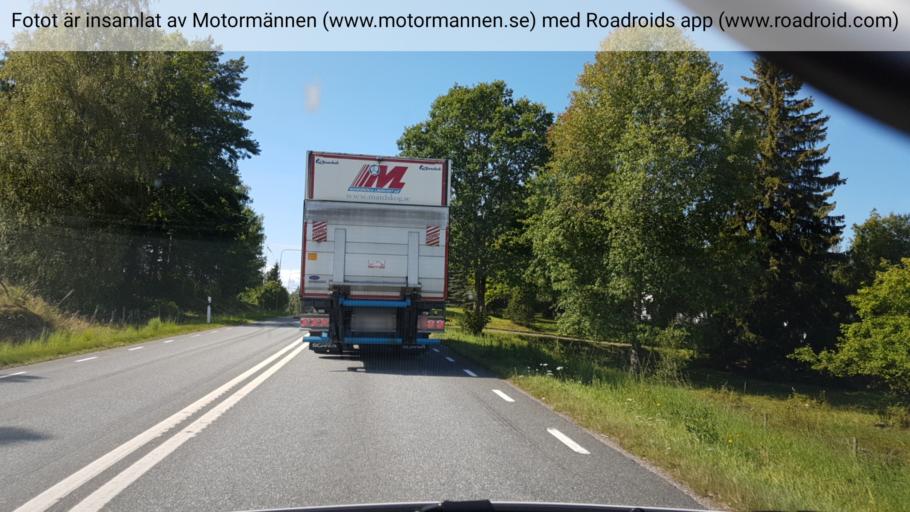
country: SE
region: Joenkoeping
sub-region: Jonkopings Kommun
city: Asa
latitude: 58.0073
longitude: 14.5843
